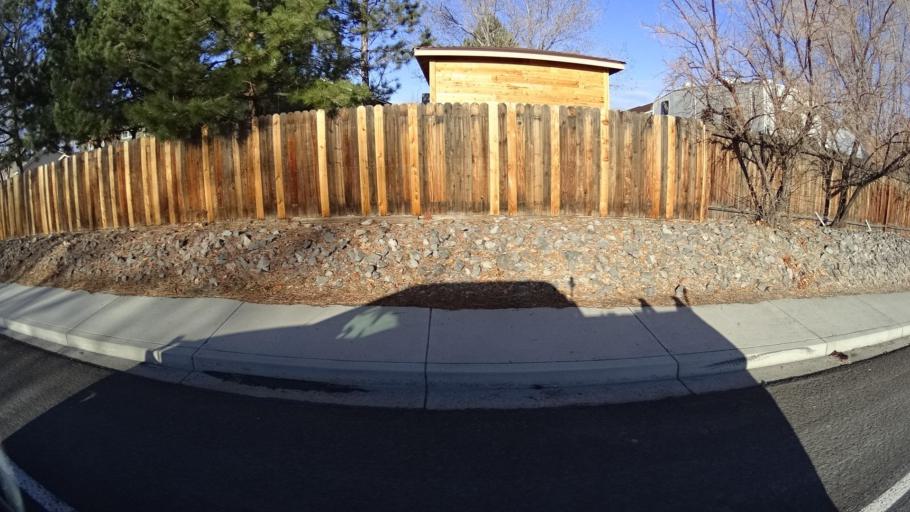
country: US
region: Nevada
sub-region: Washoe County
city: Cold Springs
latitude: 39.6801
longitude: -119.9788
